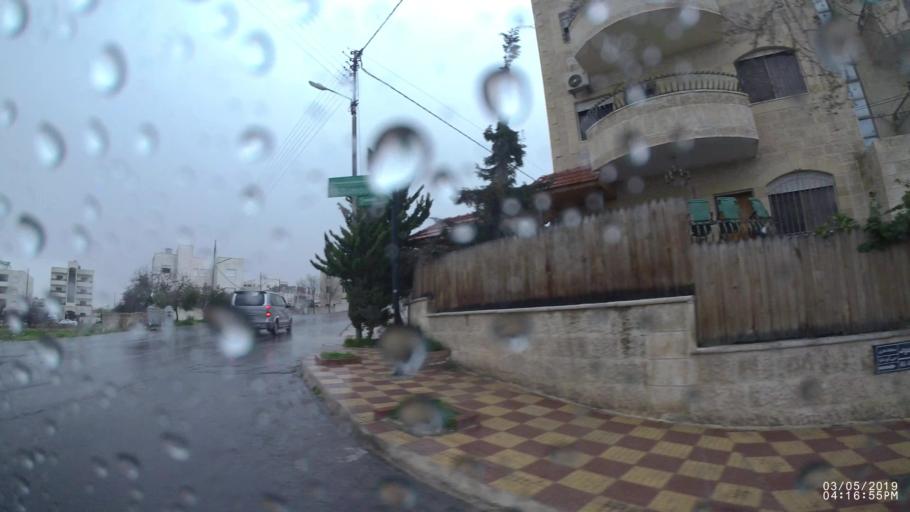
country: JO
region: Amman
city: Amman
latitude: 32.0033
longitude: 35.9542
